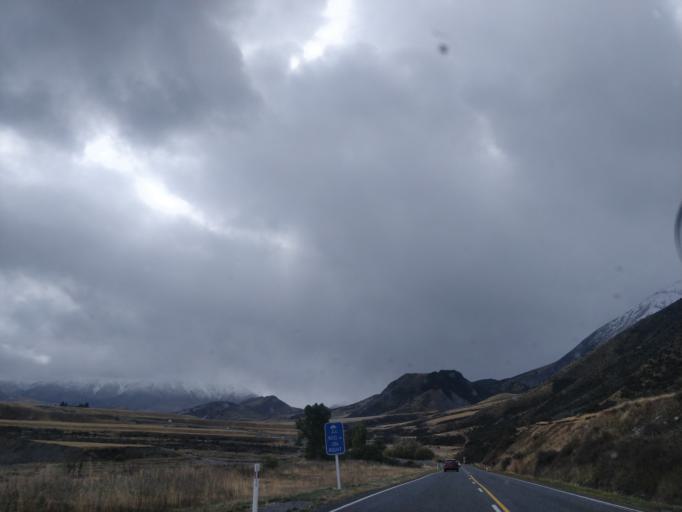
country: NZ
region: Canterbury
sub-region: Ashburton District
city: Methven
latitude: -43.2476
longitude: 171.7218
